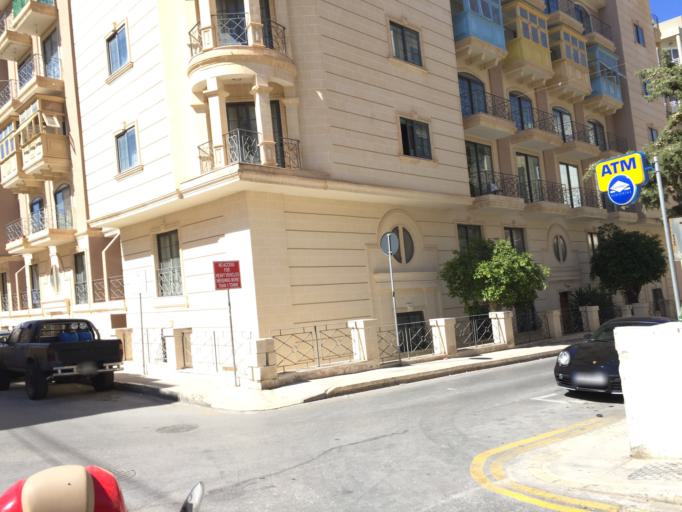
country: MT
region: Tas-Sliema
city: Sliema
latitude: 35.9126
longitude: 14.4964
